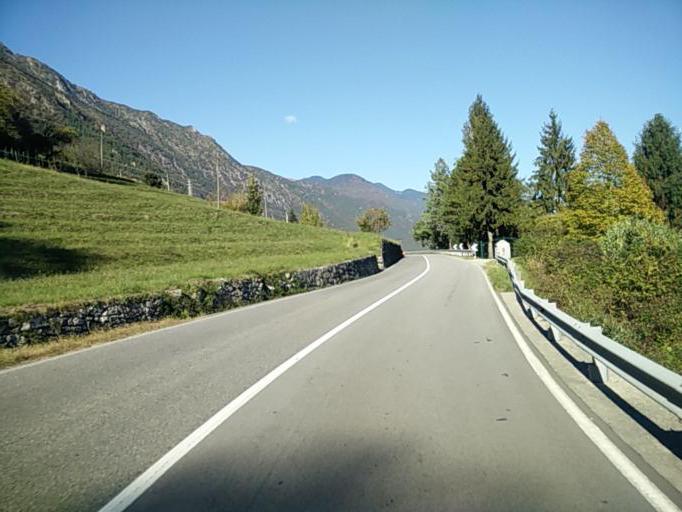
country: IT
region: Lombardy
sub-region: Provincia di Brescia
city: Anfo
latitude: 45.7844
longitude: 10.5006
